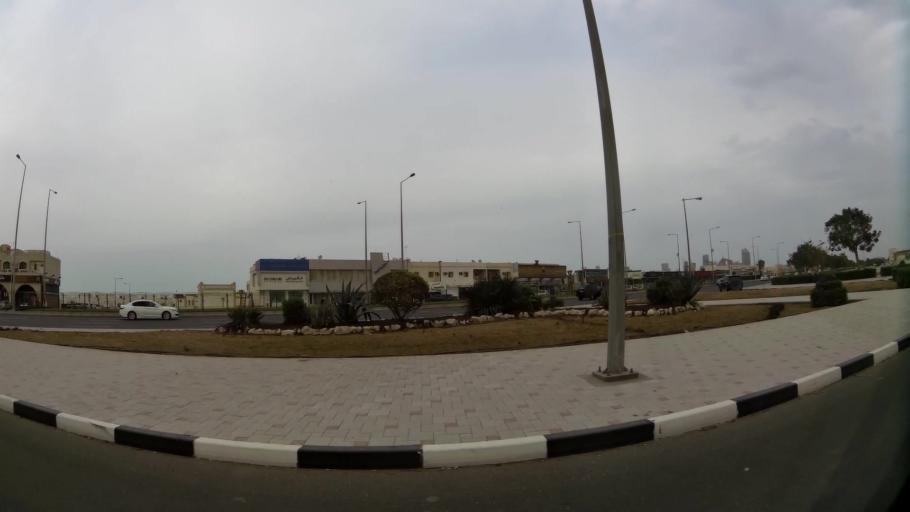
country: QA
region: Baladiyat ad Dawhah
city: Doha
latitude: 25.3204
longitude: 51.4899
